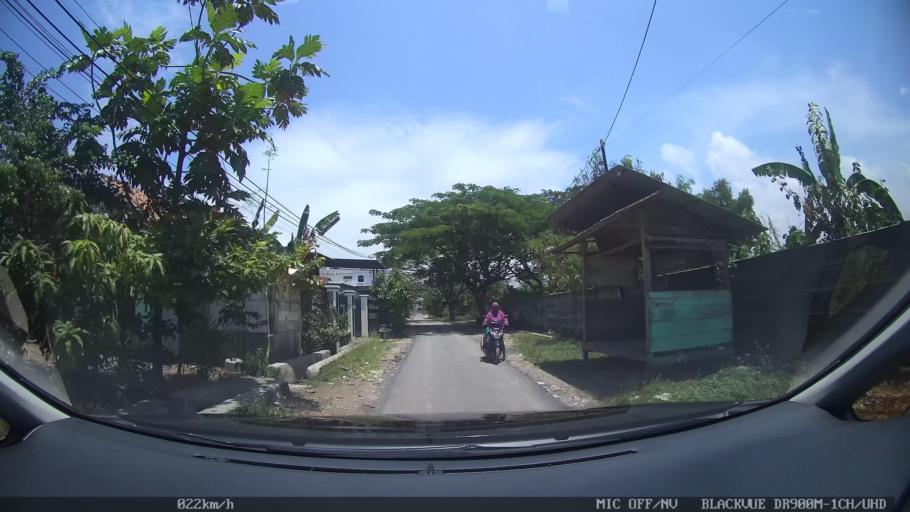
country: ID
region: Lampung
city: Kedaton
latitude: -5.3725
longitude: 105.2868
